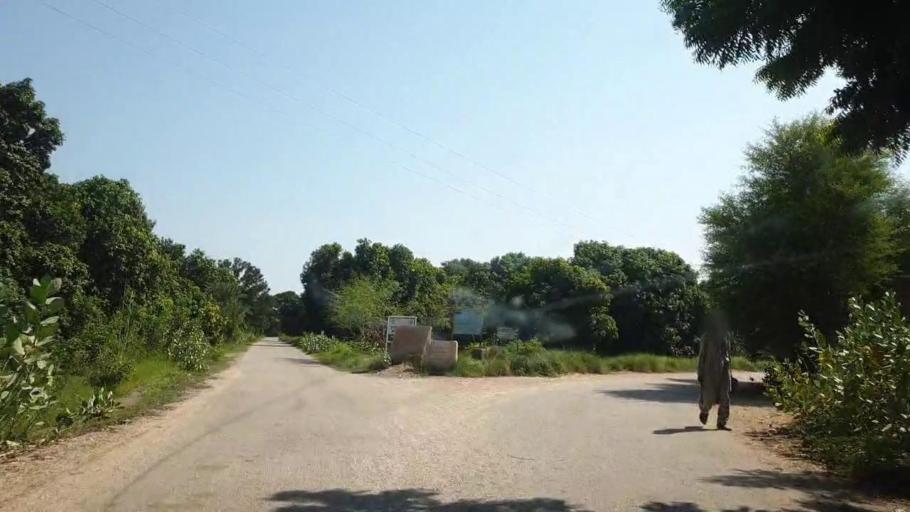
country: PK
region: Sindh
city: Tando Jam
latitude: 25.4388
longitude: 68.5847
